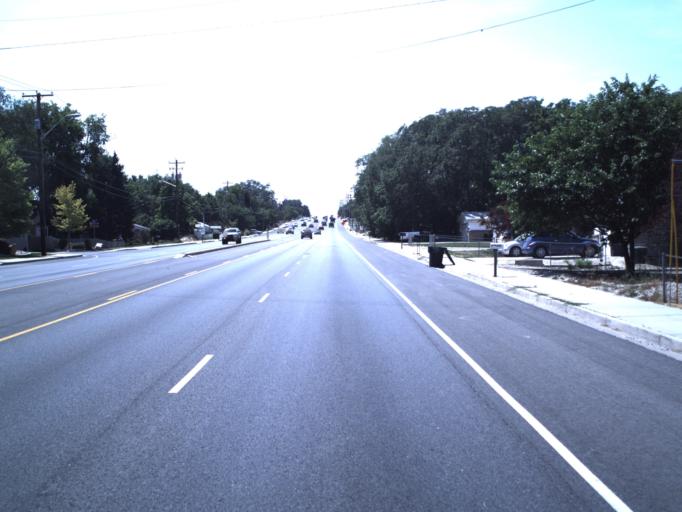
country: US
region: Utah
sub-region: Salt Lake County
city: West Valley City
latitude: 40.6938
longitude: -112.0249
